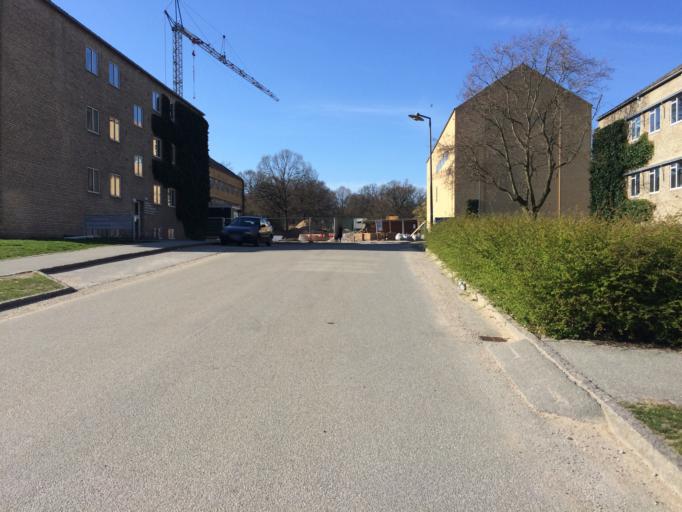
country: DK
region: Central Jutland
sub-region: Arhus Kommune
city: Arhus
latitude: 56.1659
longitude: 10.2055
